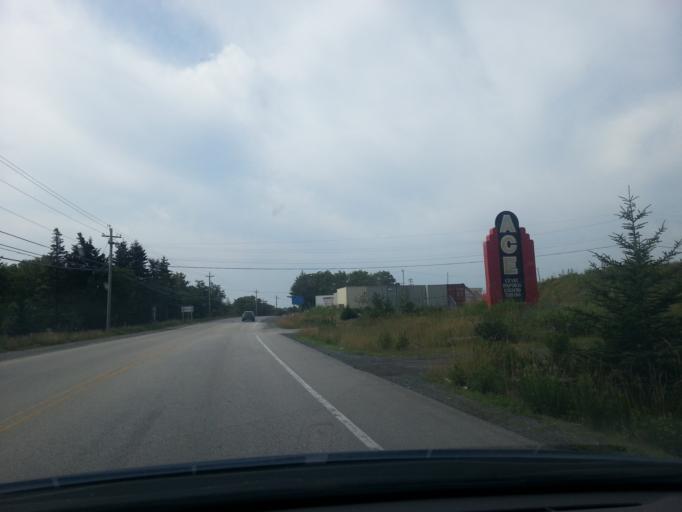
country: CA
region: Nova Scotia
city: Halifax
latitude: 44.6057
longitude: -63.6728
